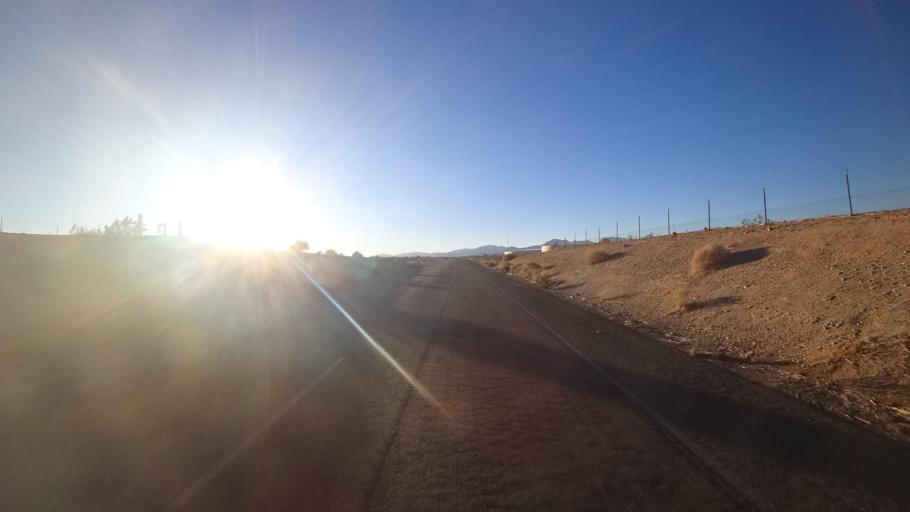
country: US
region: California
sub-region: Kern County
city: Ridgecrest
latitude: 35.6080
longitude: -117.7086
